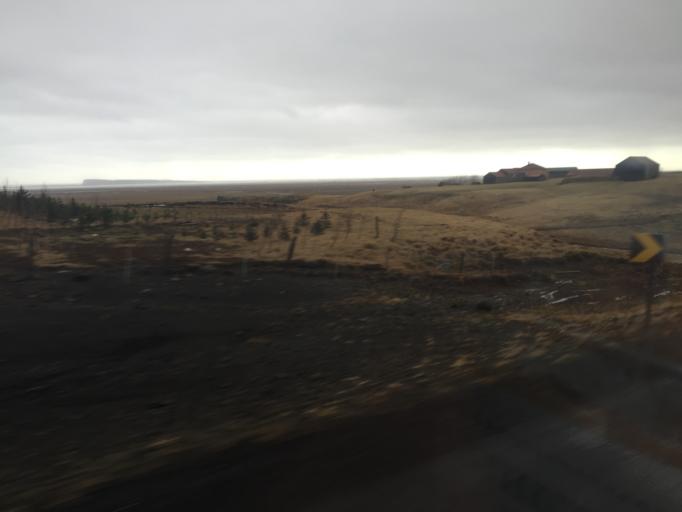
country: IS
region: East
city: Hoefn
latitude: 63.8807
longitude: -16.6388
